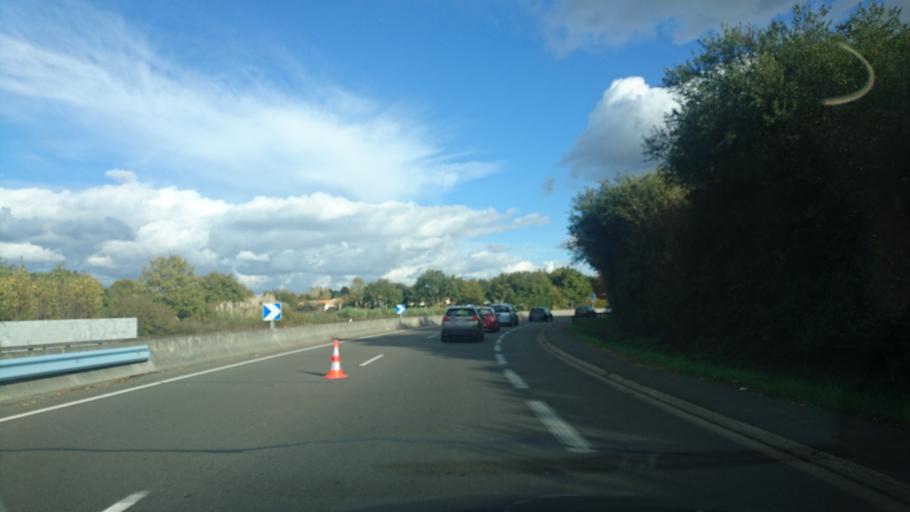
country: FR
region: Pays de la Loire
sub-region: Departement de la Vendee
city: Olonne-sur-Mer
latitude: 46.5168
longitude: -1.7620
